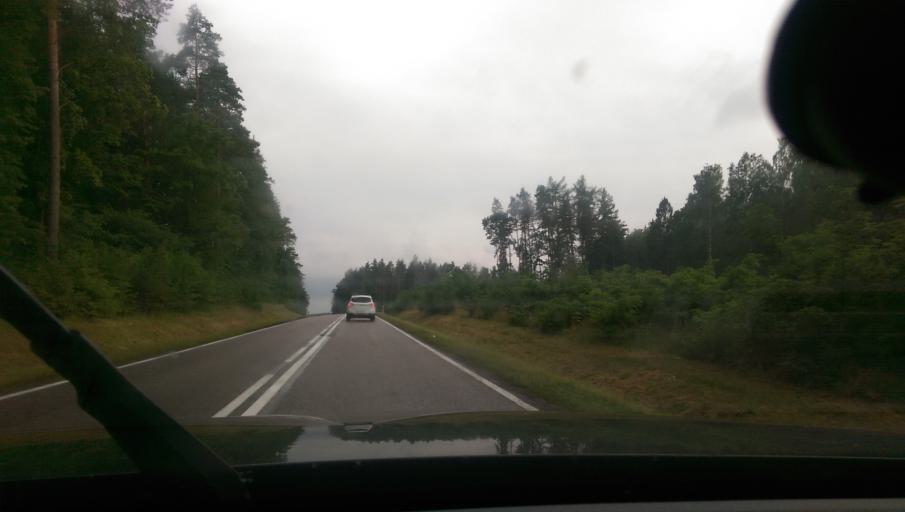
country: PL
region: Warmian-Masurian Voivodeship
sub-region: Powiat szczycienski
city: Szczytno
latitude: 53.5094
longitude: 20.9713
